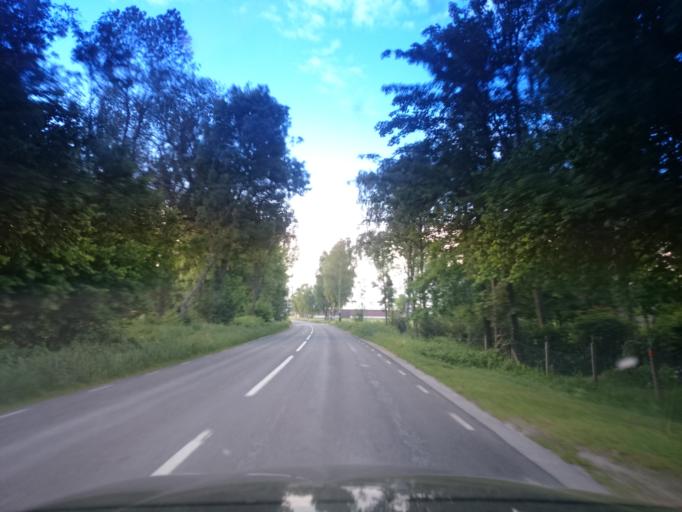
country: SE
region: Gotland
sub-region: Gotland
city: Hemse
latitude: 57.3174
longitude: 18.3851
